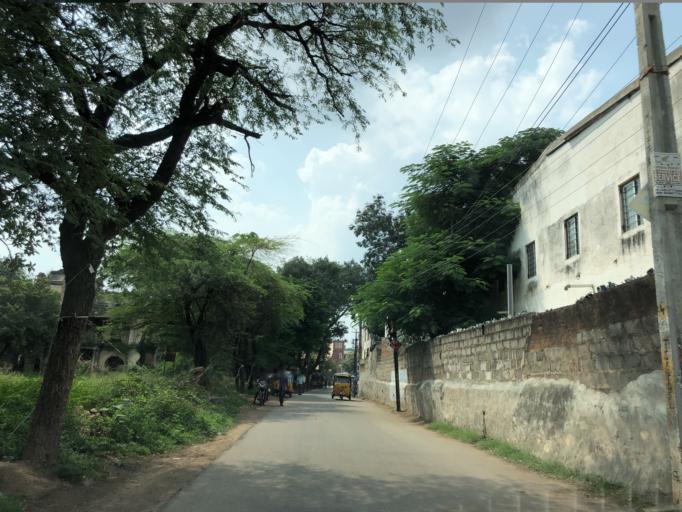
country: IN
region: Telangana
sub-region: Hyderabad
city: Malkajgiri
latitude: 17.4458
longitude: 78.4863
